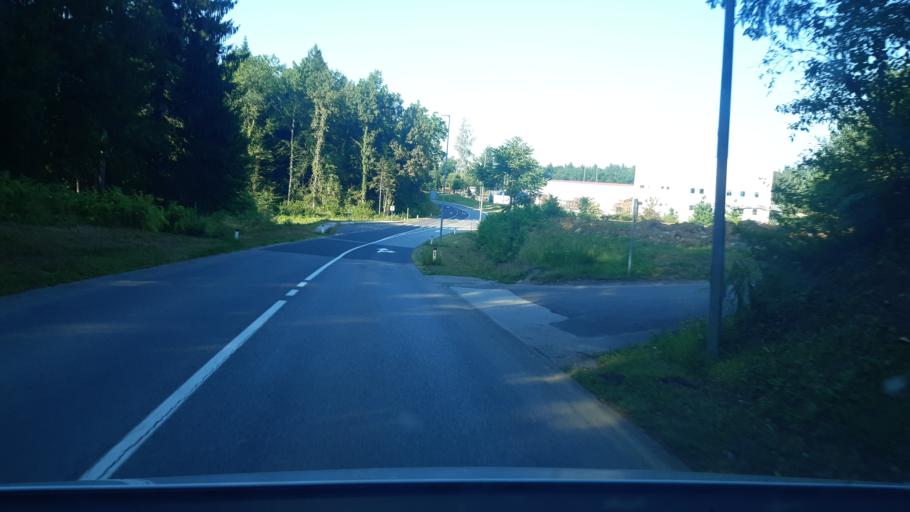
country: SI
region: Crnomelj
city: Crnomelj
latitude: 45.5567
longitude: 15.1667
